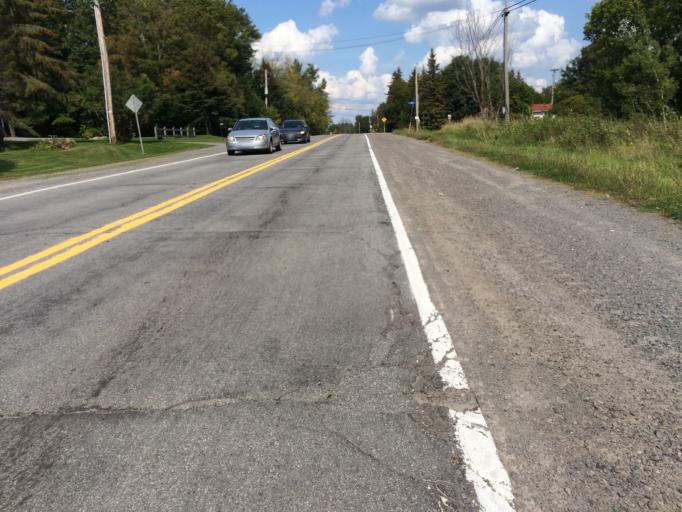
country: CA
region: Ontario
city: Bells Corners
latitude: 45.1641
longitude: -75.6423
